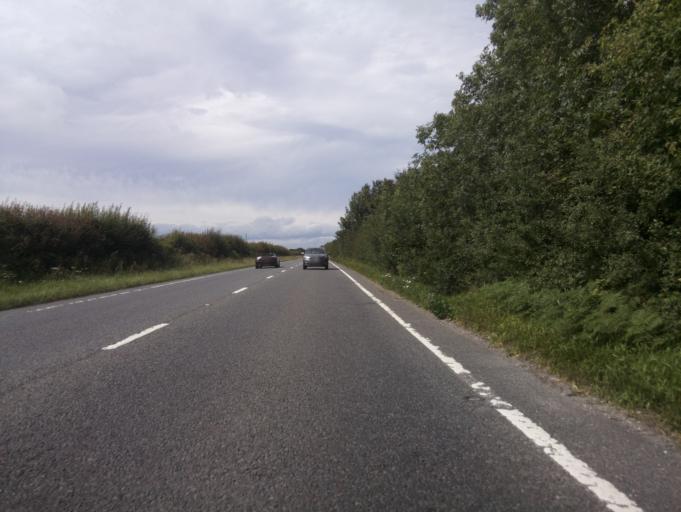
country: GB
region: England
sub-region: Dorset
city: Sherborne
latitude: 50.8077
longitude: -2.5527
